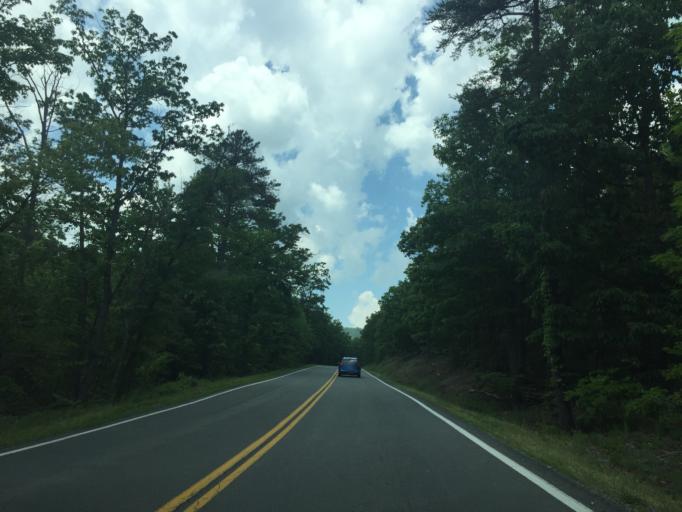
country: US
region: Virginia
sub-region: Shenandoah County
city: Strasburg
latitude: 39.0930
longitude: -78.4402
